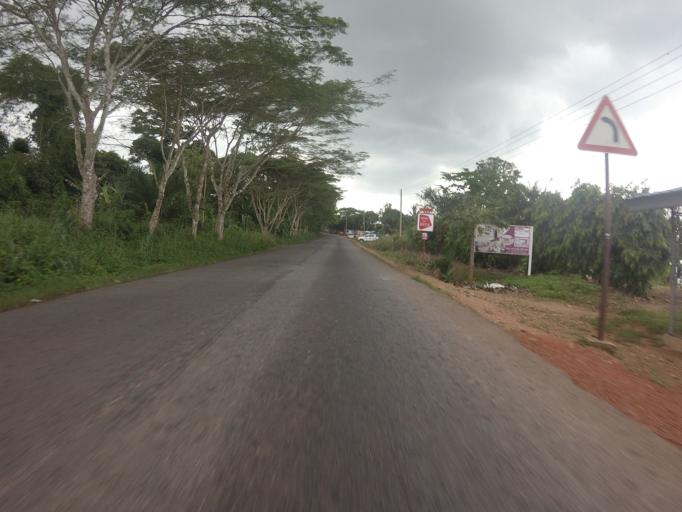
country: GH
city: Akropong
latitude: 5.9443
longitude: -0.1189
